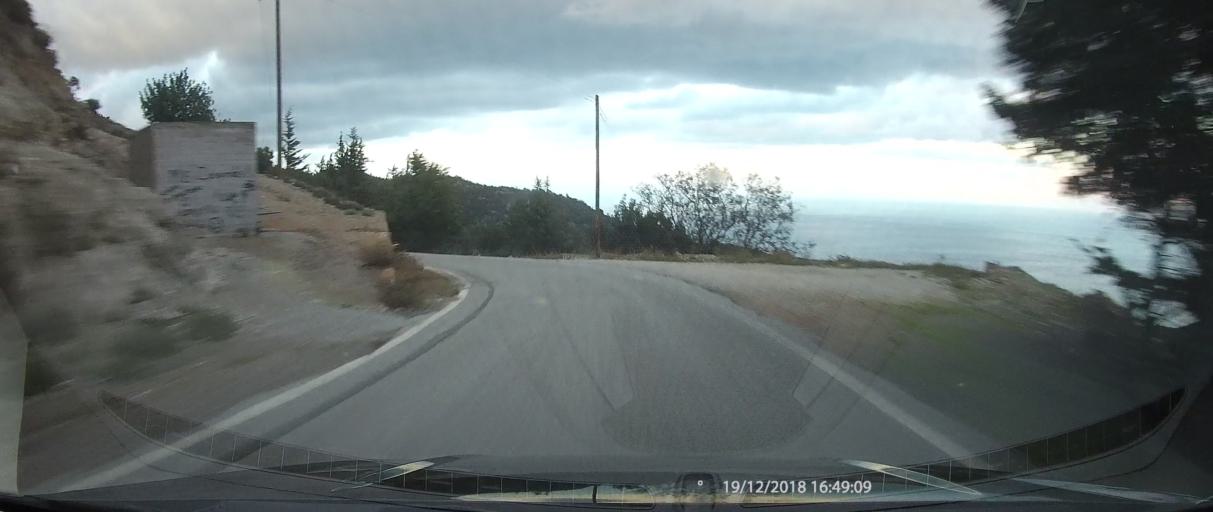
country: GR
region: Peloponnese
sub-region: Nomos Lakonias
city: Sykea
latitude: 36.9432
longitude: 22.9961
